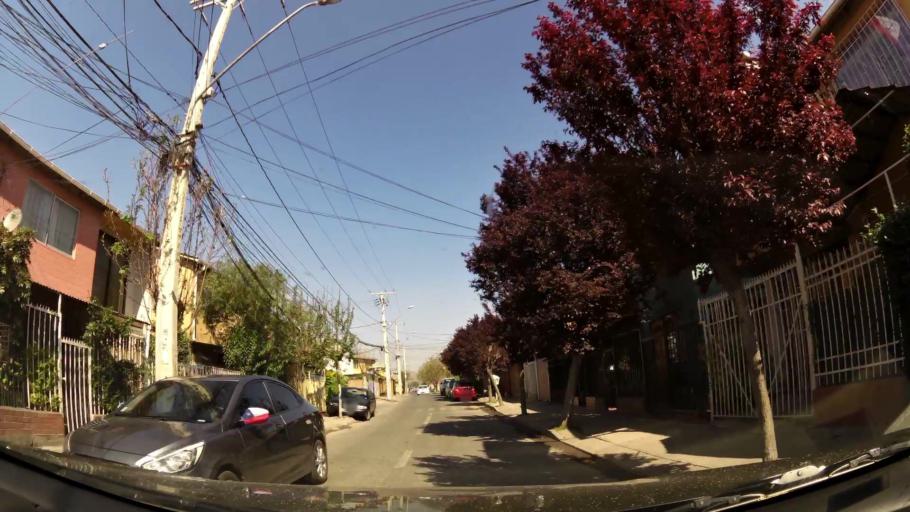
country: CL
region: Santiago Metropolitan
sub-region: Provincia de Santiago
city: Lo Prado
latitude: -33.3576
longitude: -70.7510
